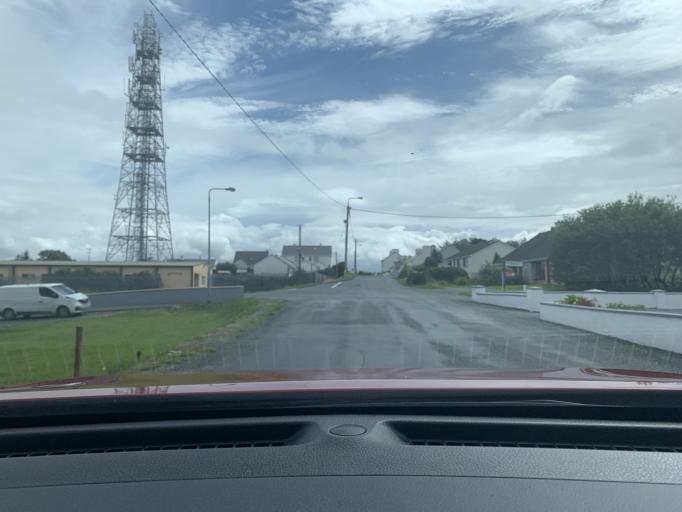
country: IE
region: Ulster
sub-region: County Donegal
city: Dungloe
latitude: 54.9546
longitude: -8.3639
